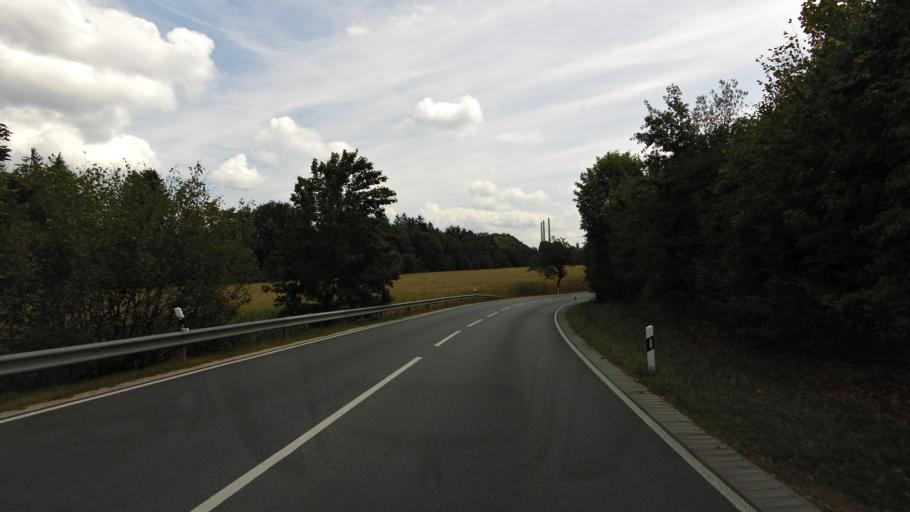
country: DE
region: Bavaria
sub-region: Upper Bavaria
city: Unterneukirchen
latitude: 48.1520
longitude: 12.6127
